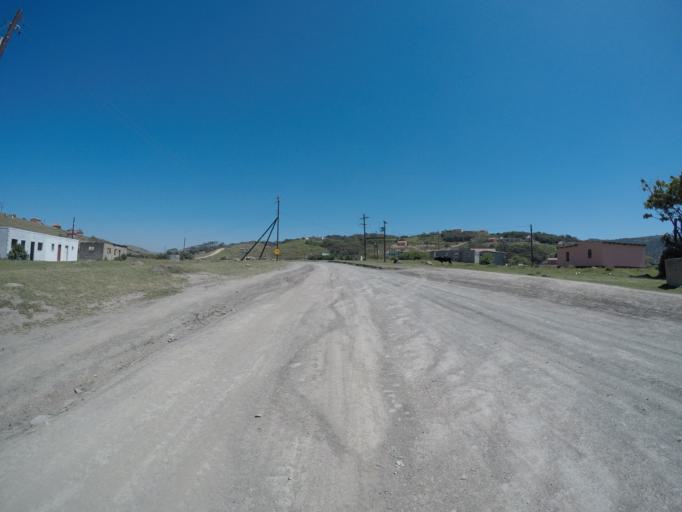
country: ZA
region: Eastern Cape
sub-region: OR Tambo District Municipality
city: Libode
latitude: -32.0314
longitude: 29.1086
